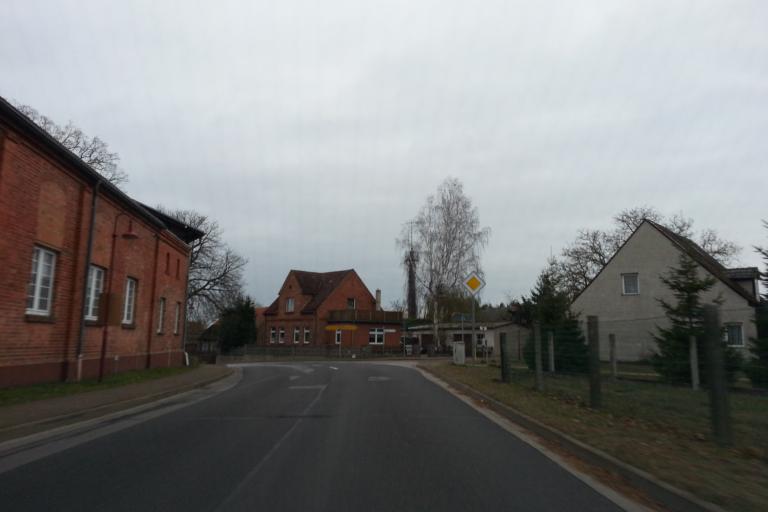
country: DE
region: Mecklenburg-Vorpommern
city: Ferdinandshof
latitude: 53.5948
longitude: 13.8226
